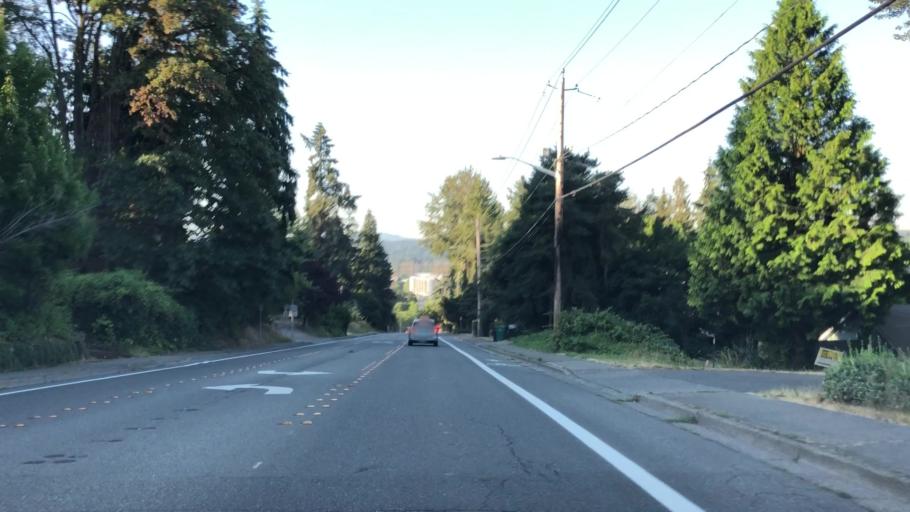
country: US
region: Washington
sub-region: King County
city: Redmond
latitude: 47.6824
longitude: -122.1192
